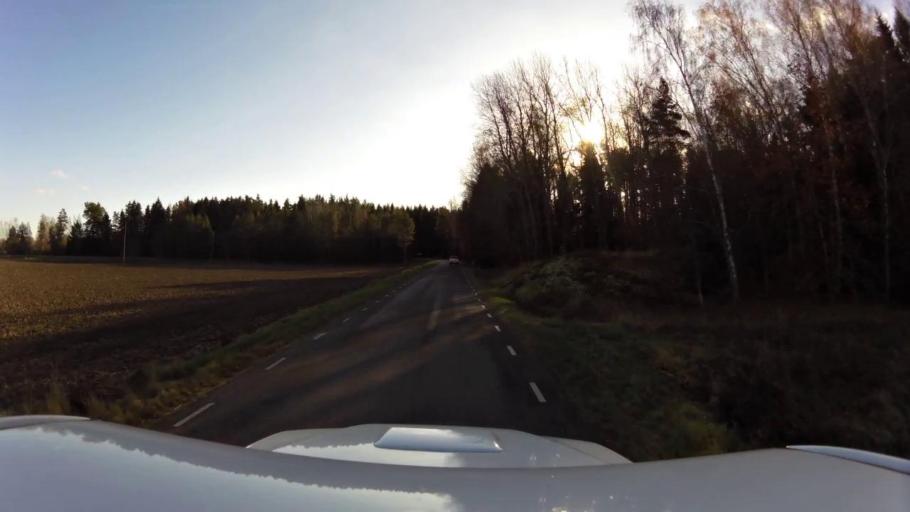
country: SE
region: OEstergoetland
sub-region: Linkopings Kommun
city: Linghem
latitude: 58.4606
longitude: 15.7750
